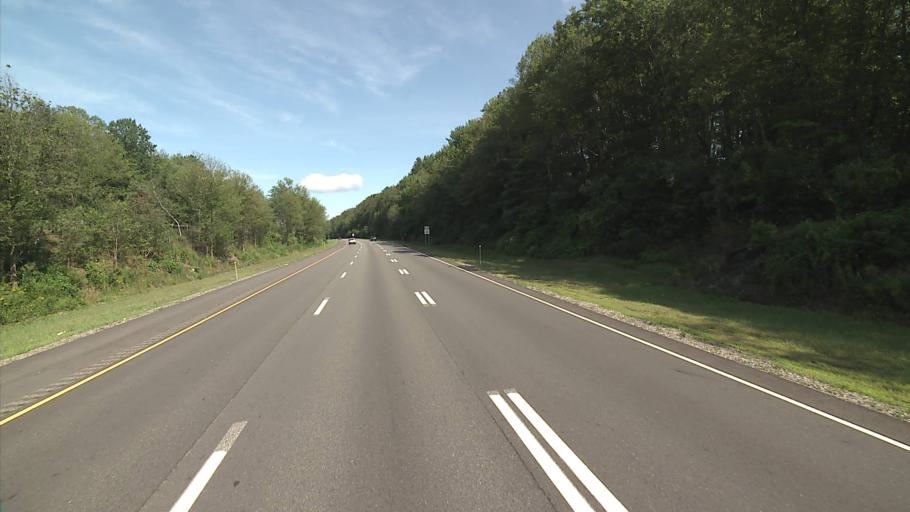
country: US
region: Connecticut
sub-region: Hartford County
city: Terramuggus
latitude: 41.6397
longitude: -72.4618
